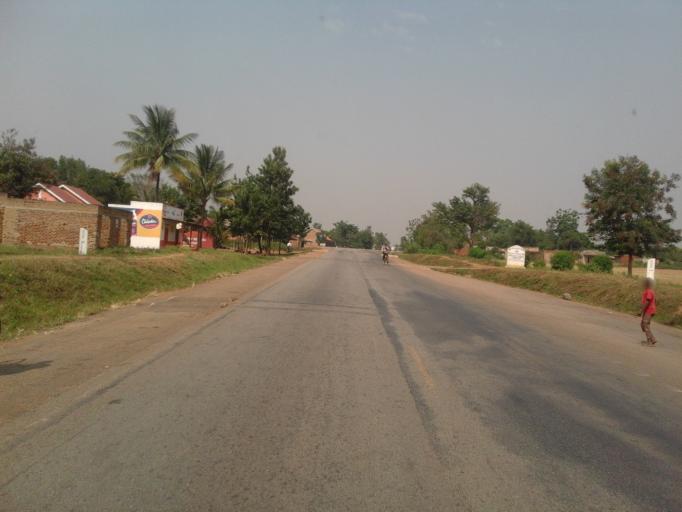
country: UG
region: Eastern Region
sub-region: Bugiri District
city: Bugiri
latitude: 0.6211
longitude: 33.6322
